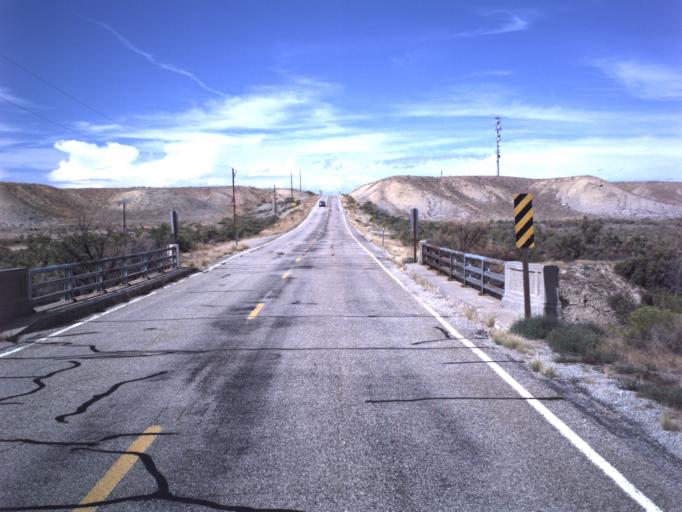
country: US
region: Utah
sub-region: Grand County
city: Moab
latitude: 38.9375
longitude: -109.3980
